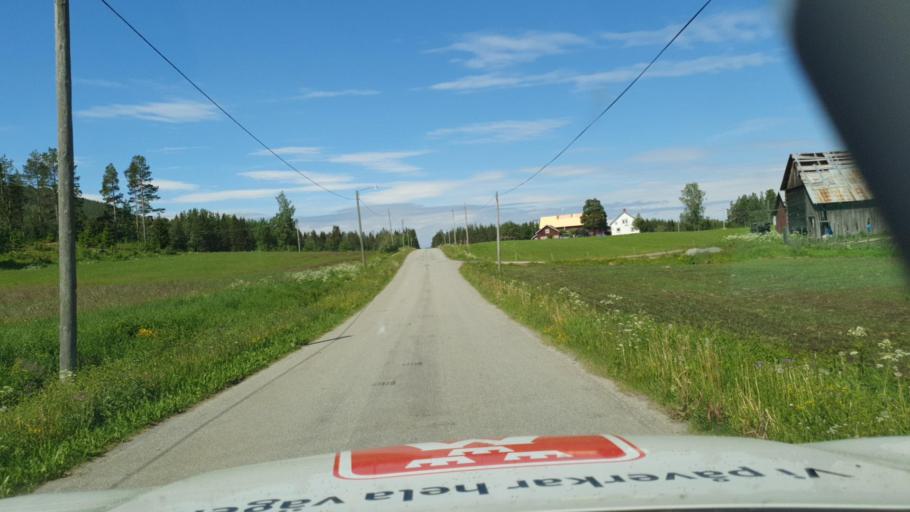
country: SE
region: Jaemtland
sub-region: Bergs Kommun
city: Hoverberg
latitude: 62.8362
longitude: 14.4502
